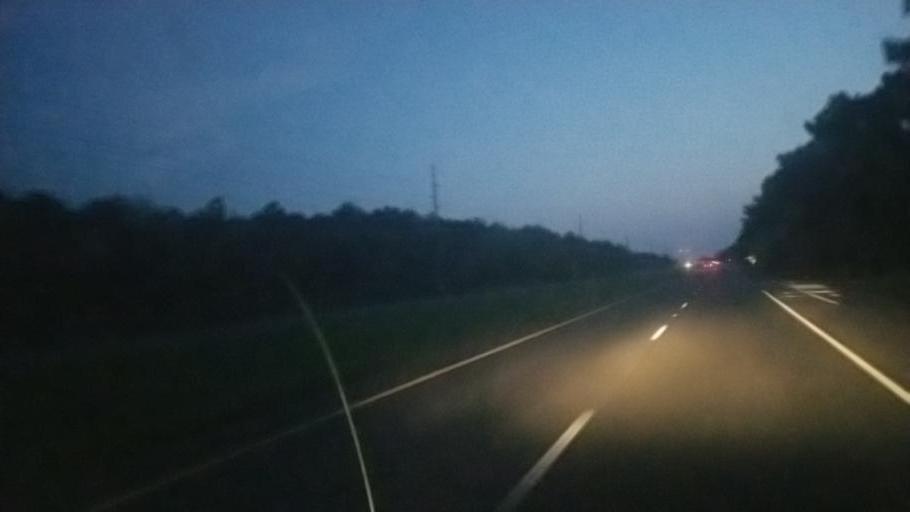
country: US
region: Delaware
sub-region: Sussex County
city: Bethany Beach
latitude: 38.5723
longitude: -75.0604
